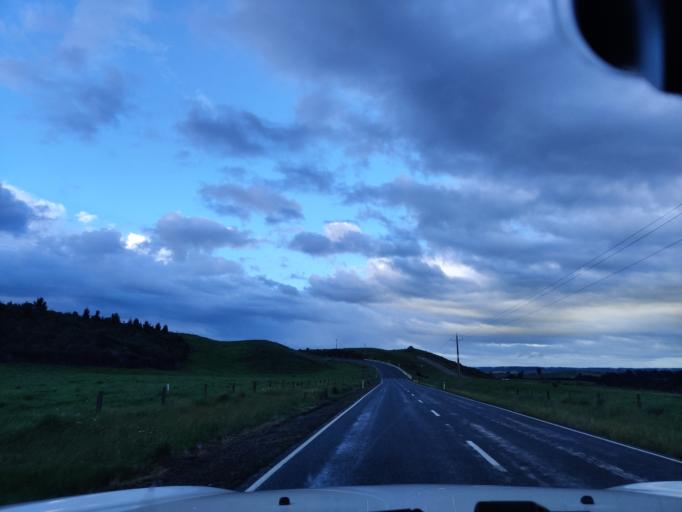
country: NZ
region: Waikato
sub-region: South Waikato District
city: Tokoroa
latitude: -38.3838
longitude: 175.7837
